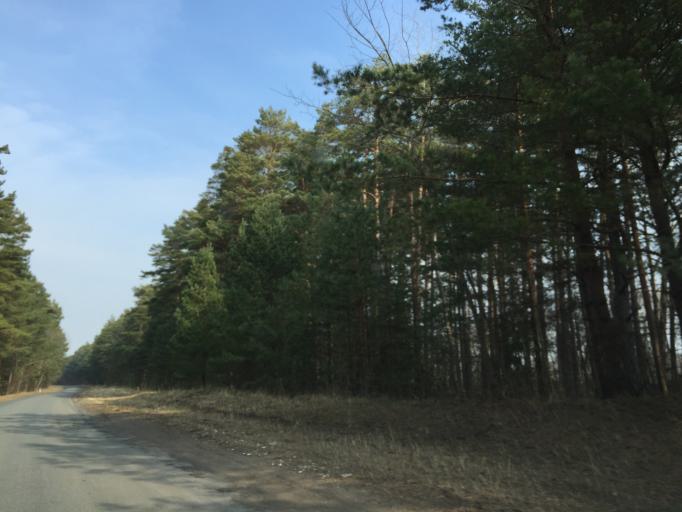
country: LV
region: Salacgrivas
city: Ainazi
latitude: 57.8901
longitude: 24.3692
